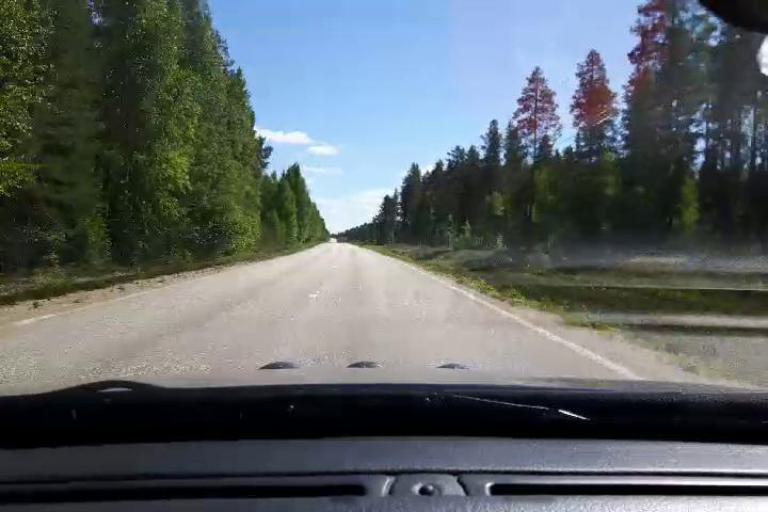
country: SE
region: Jaemtland
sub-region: Harjedalens Kommun
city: Sveg
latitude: 62.1010
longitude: 15.0723
